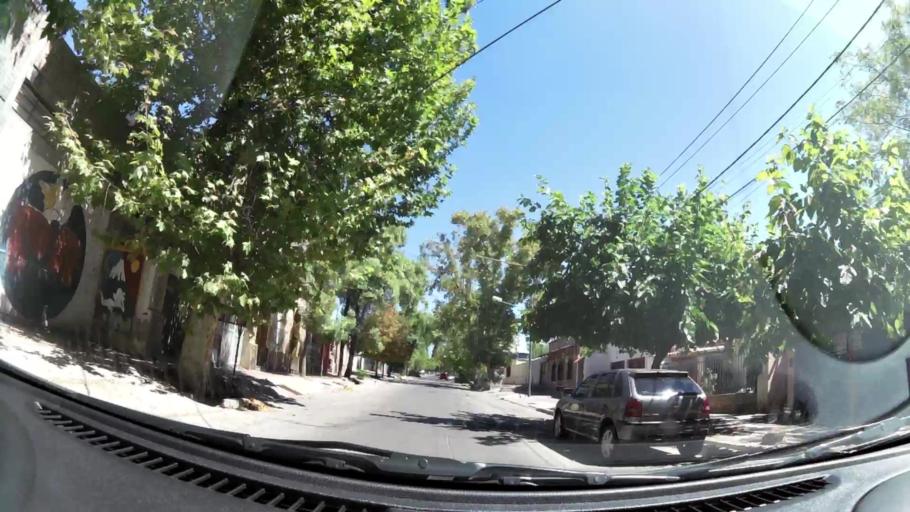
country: AR
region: Mendoza
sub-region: Departamento de Godoy Cruz
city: Godoy Cruz
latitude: -32.9098
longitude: -68.8624
